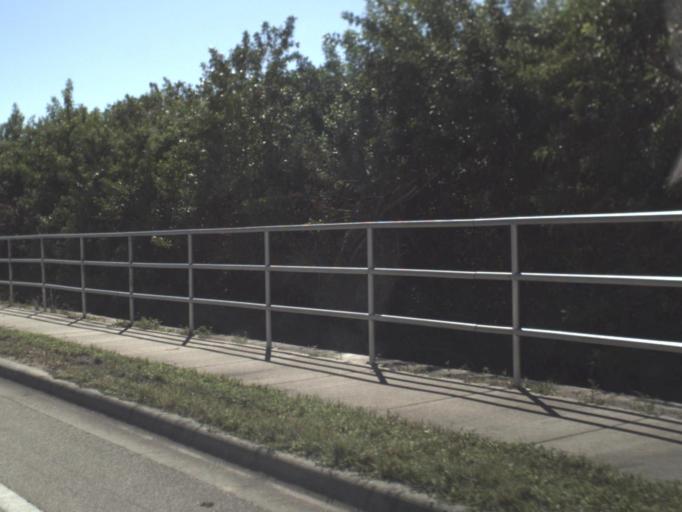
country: US
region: Florida
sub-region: Sarasota County
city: North Port
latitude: 26.9635
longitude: -82.2114
